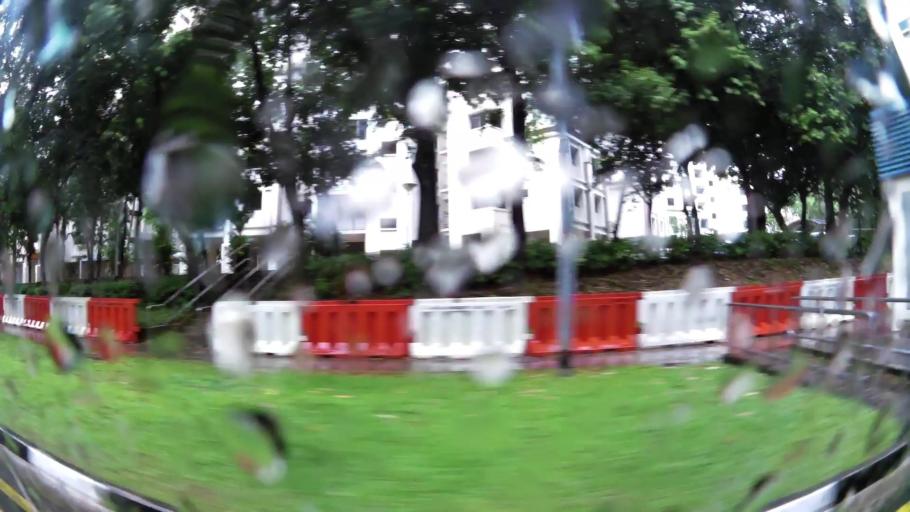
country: MY
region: Johor
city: Kampung Pasir Gudang Baru
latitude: 1.3881
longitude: 103.9053
